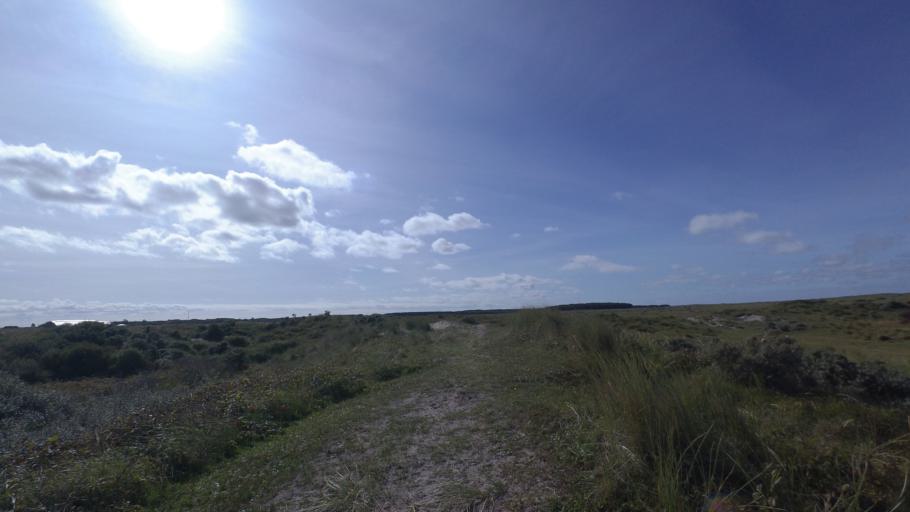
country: NL
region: Friesland
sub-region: Gemeente Ameland
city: Nes
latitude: 53.4537
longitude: 5.7319
